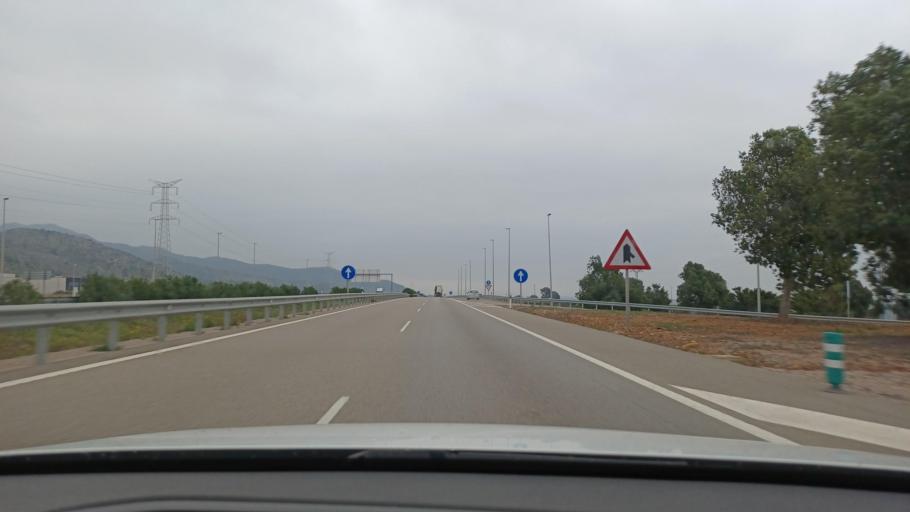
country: ES
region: Valencia
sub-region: Provincia de Castello
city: Chilches
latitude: 39.8165
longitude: -0.2117
